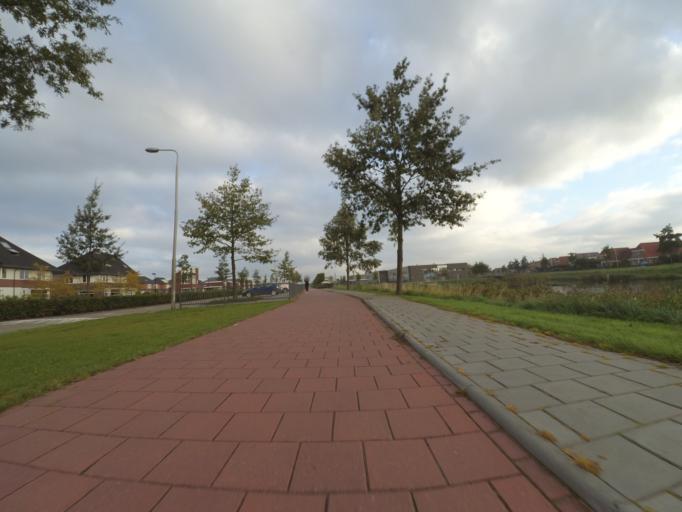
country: NL
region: Flevoland
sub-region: Gemeente Dronten
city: Dronten
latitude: 52.5334
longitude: 5.6930
